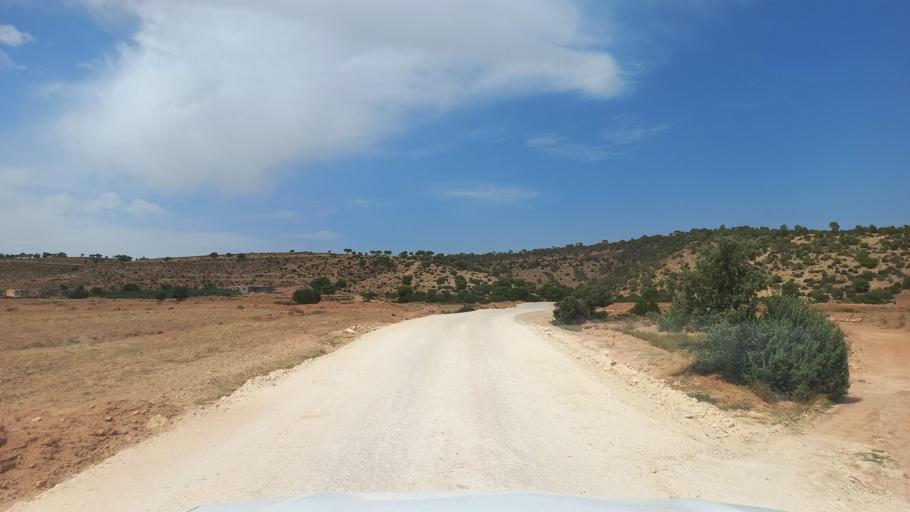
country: TN
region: Al Qasrayn
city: Kasserine
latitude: 35.3711
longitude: 8.8884
